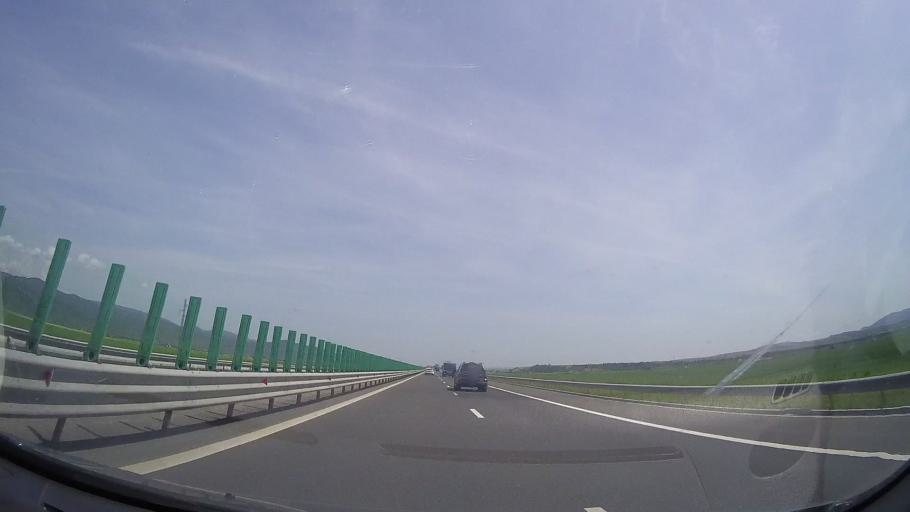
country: RO
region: Alba
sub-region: Comuna Sibot
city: Sibot
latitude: 45.9119
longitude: 23.3195
